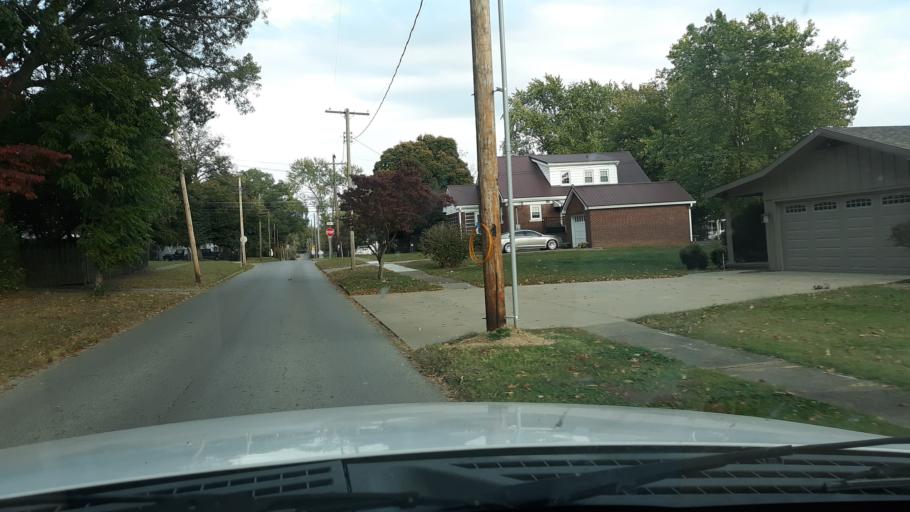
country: US
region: Illinois
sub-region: Saline County
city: Eldorado
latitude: 37.8161
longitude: -88.4394
